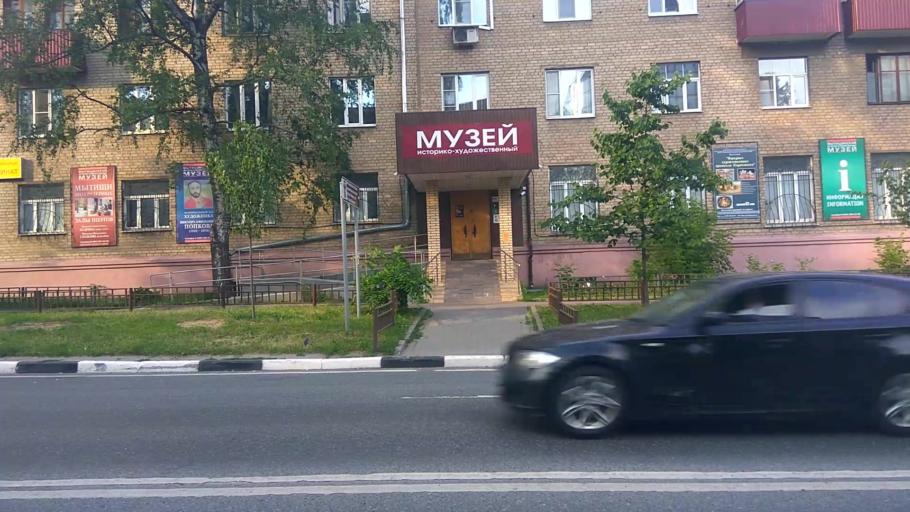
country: RU
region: Moskovskaya
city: Mytishchi
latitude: 55.9112
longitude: 37.7350
